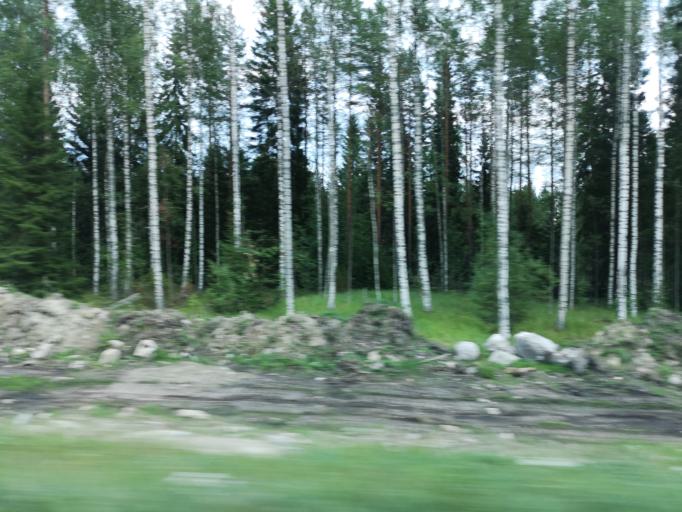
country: FI
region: Central Finland
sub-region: Joutsa
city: Leivonmaeki
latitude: 61.8407
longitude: 26.0979
